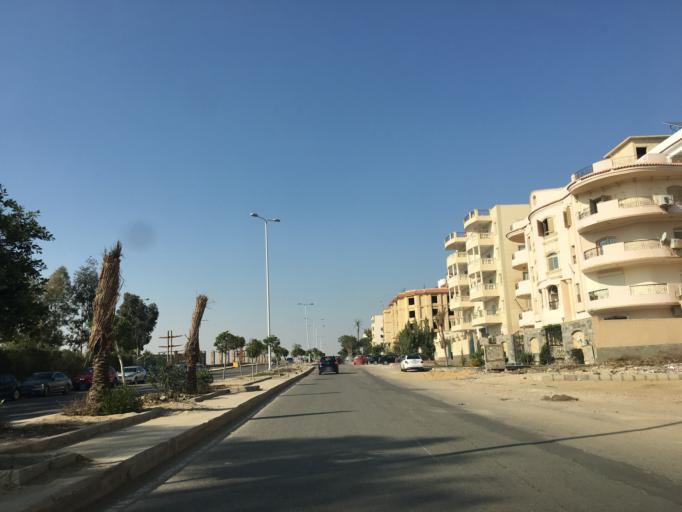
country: EG
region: Al Jizah
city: Madinat Sittah Uktubar
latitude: 29.9986
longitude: 30.9759
